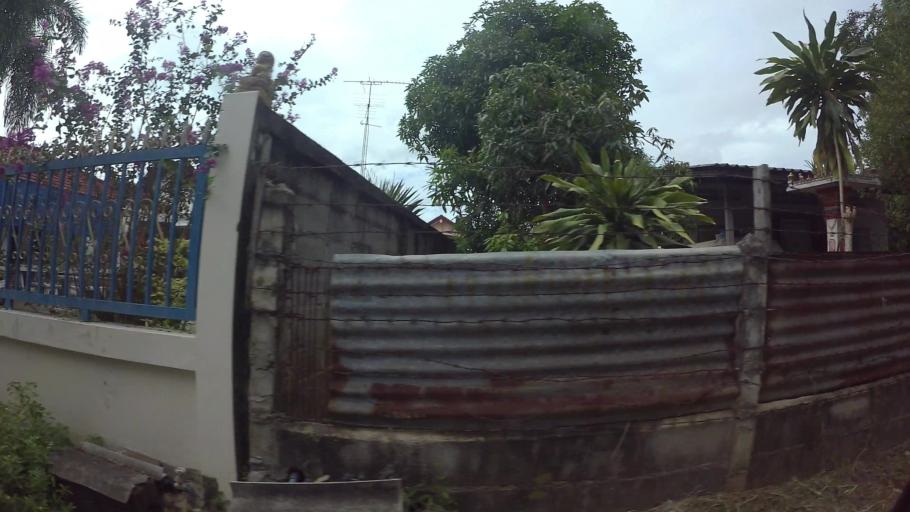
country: TH
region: Chon Buri
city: Sattahip
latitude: 12.7069
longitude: 100.8947
